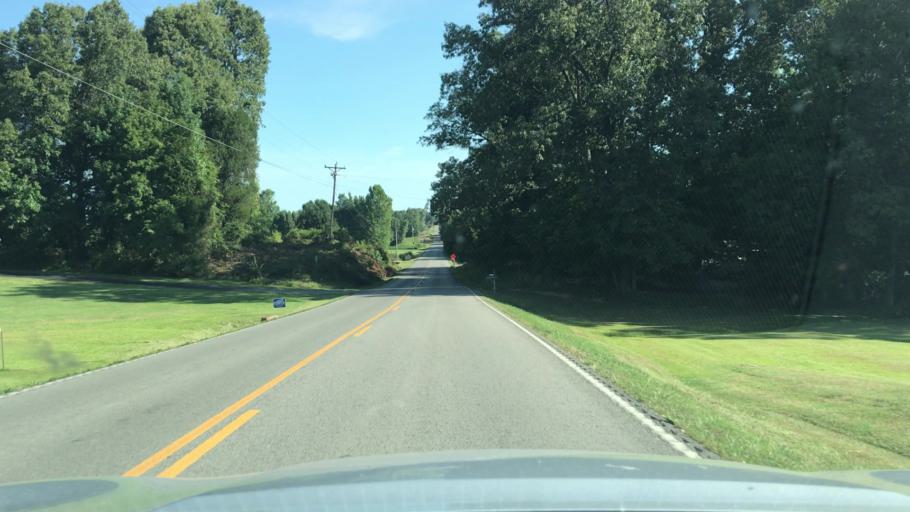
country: US
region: Kentucky
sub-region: Muhlenberg County
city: Greenville
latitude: 37.1485
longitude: -87.1413
